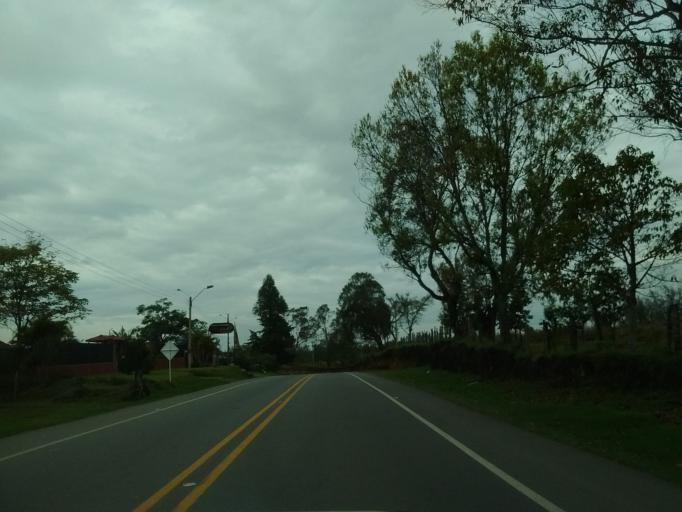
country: CO
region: Cauca
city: Popayan
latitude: 2.5166
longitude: -76.5432
